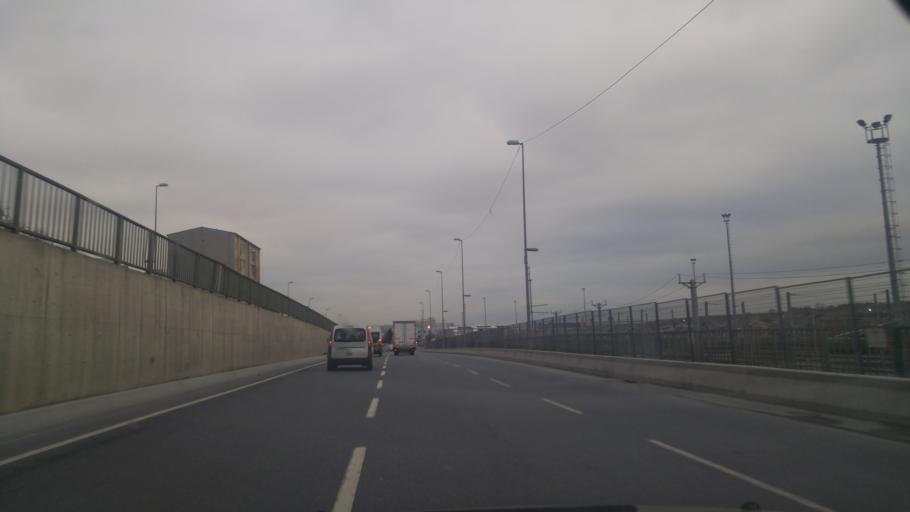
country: TR
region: Istanbul
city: Mahmutbey
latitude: 41.0243
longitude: 28.7674
